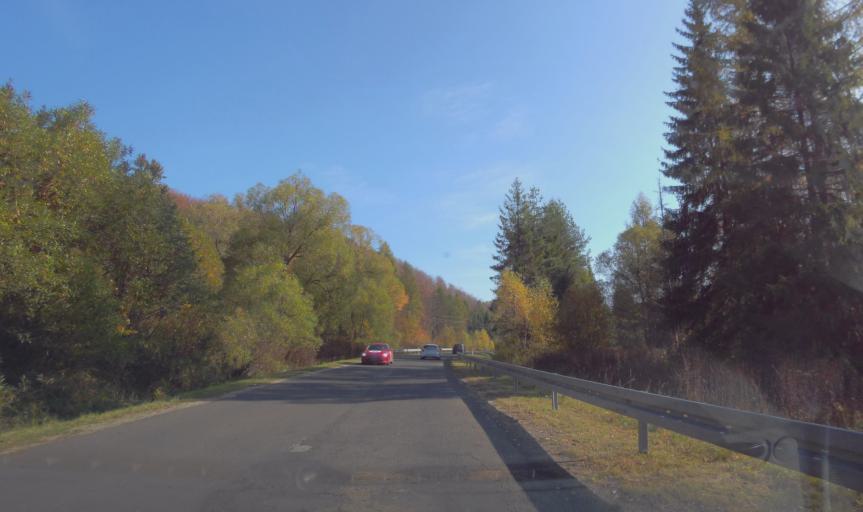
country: PL
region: Subcarpathian Voivodeship
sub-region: Powiat leski
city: Cisna
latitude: 49.2185
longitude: 22.2151
